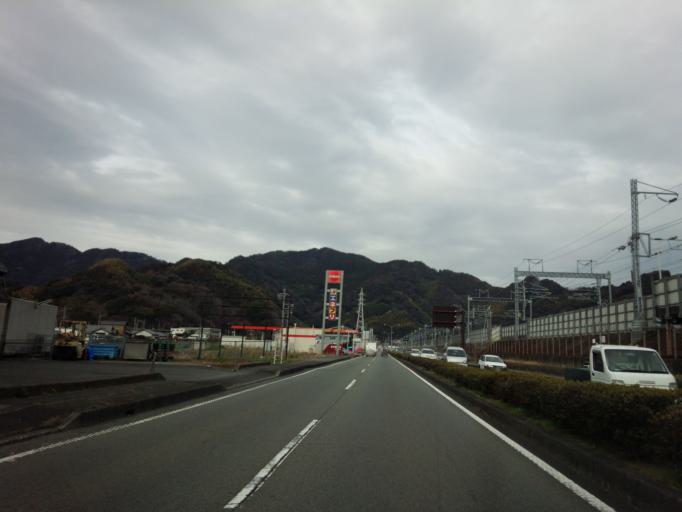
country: JP
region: Shizuoka
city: Yaizu
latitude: 34.8886
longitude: 138.3270
